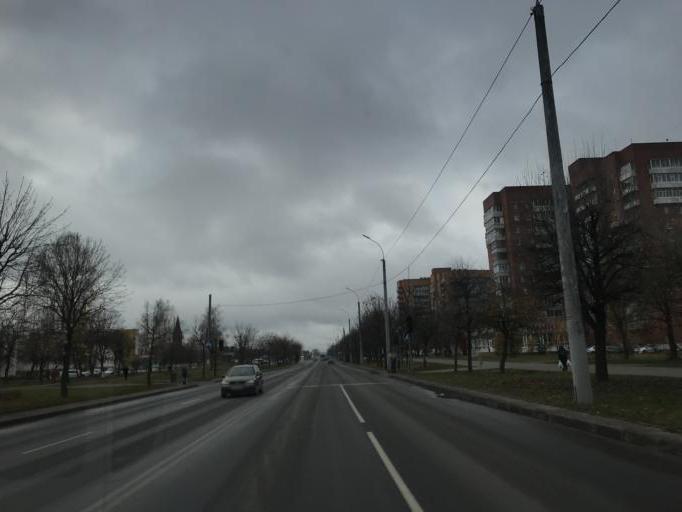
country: BY
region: Mogilev
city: Mahilyow
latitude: 53.8727
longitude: 30.3280
